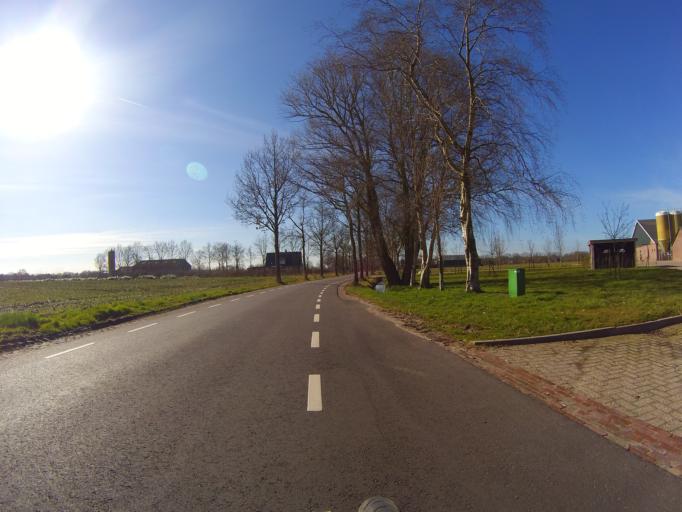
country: NL
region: Utrecht
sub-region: Gemeente Utrechtse Heuvelrug
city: Overberg
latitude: 52.0674
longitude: 5.5076
